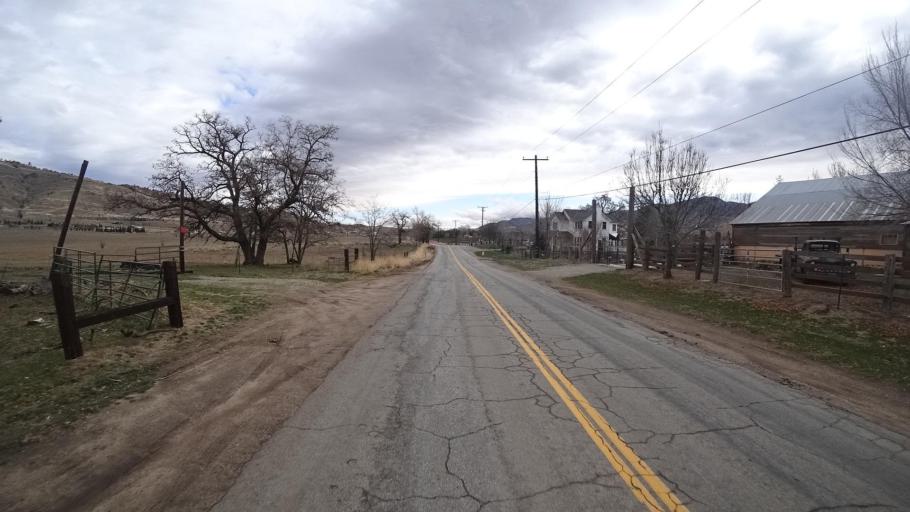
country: US
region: California
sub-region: Kern County
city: Golden Hills
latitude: 35.1181
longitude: -118.5481
